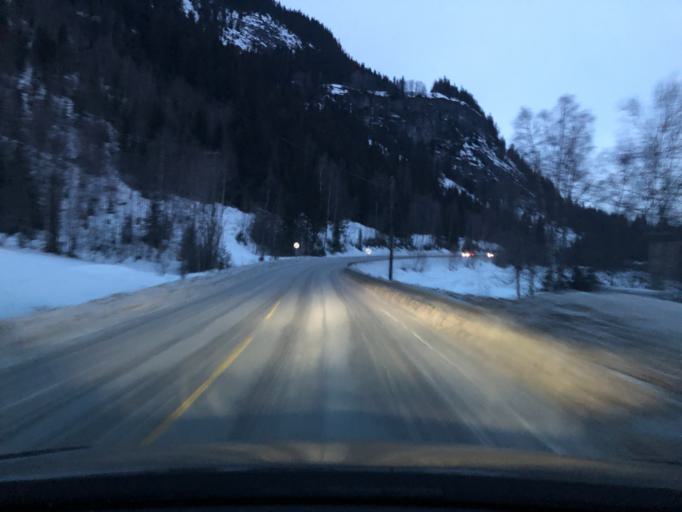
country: NO
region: Oppland
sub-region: Nord-Aurdal
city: Fagernes
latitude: 60.9979
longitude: 9.2120
